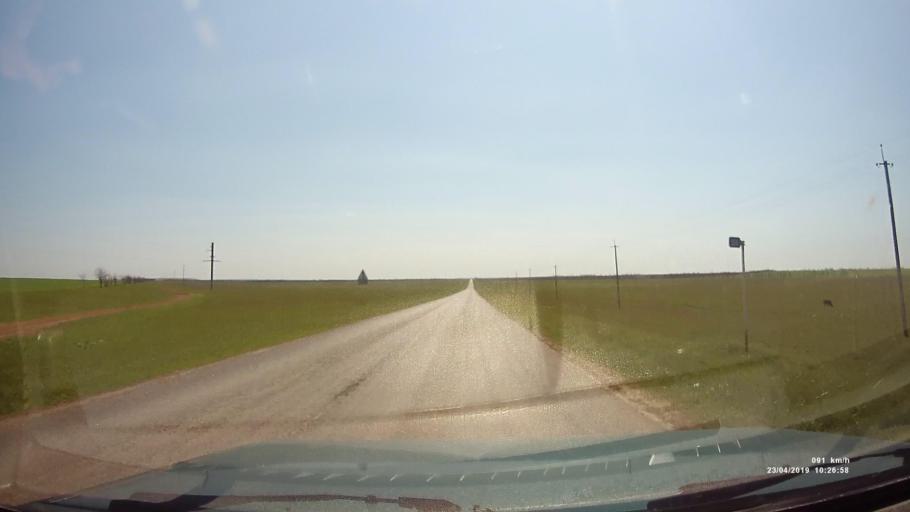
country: RU
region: Kalmykiya
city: Yashalta
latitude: 46.6170
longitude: 42.4845
